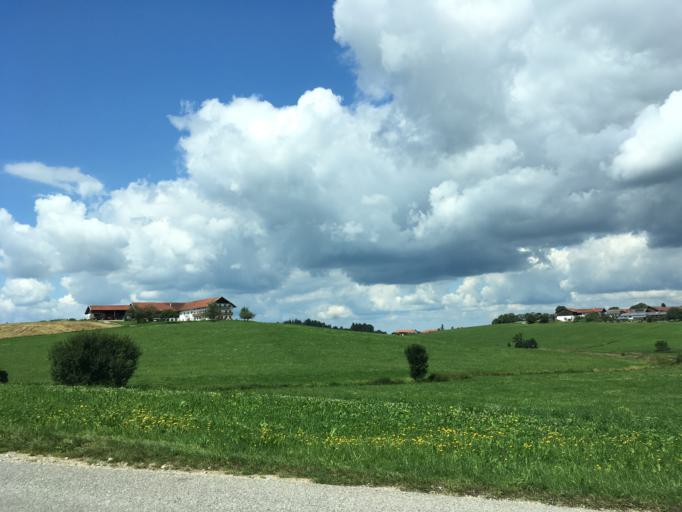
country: DE
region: Bavaria
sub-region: Upper Bavaria
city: Amerang
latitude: 47.9858
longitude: 12.3394
